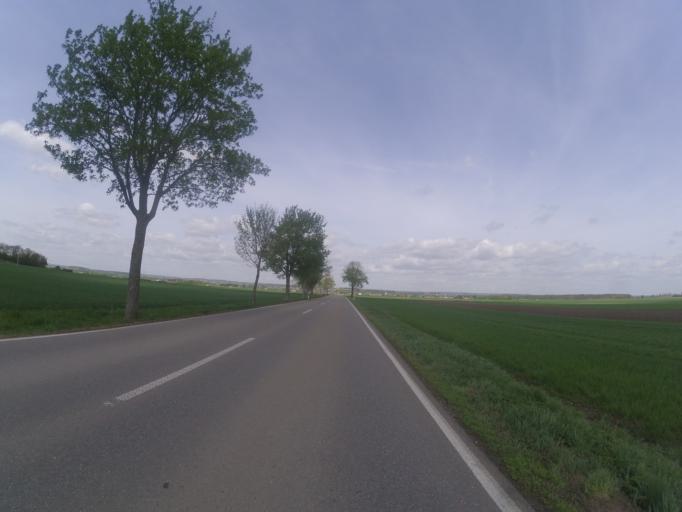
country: DE
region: Baden-Wuerttemberg
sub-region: Tuebingen Region
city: Ersingen
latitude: 48.2771
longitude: 9.8598
